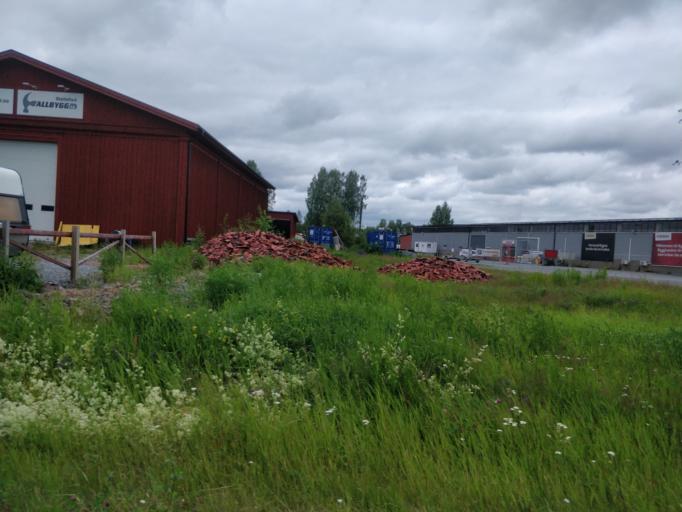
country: SE
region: Vaesterbotten
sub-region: Skelleftea Kommun
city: Viken
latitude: 64.7586
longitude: 20.8901
